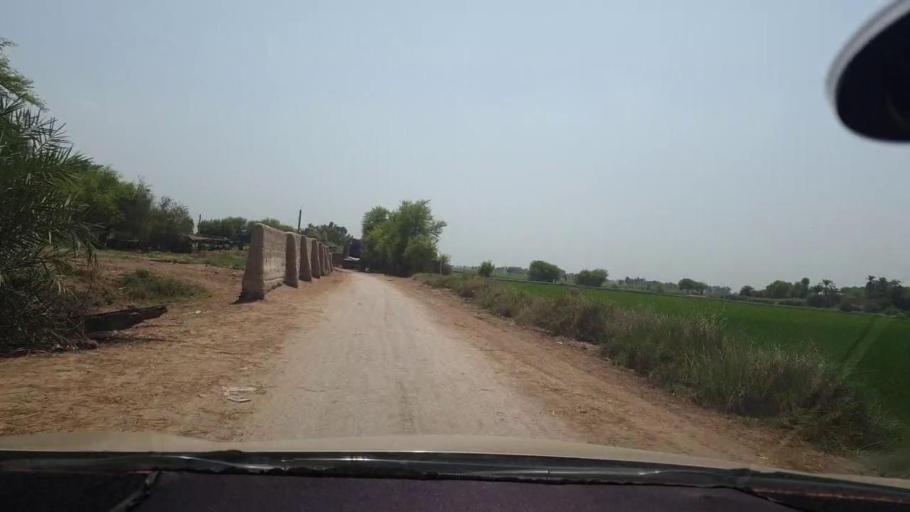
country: PK
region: Sindh
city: Kambar
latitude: 27.6593
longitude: 67.9327
